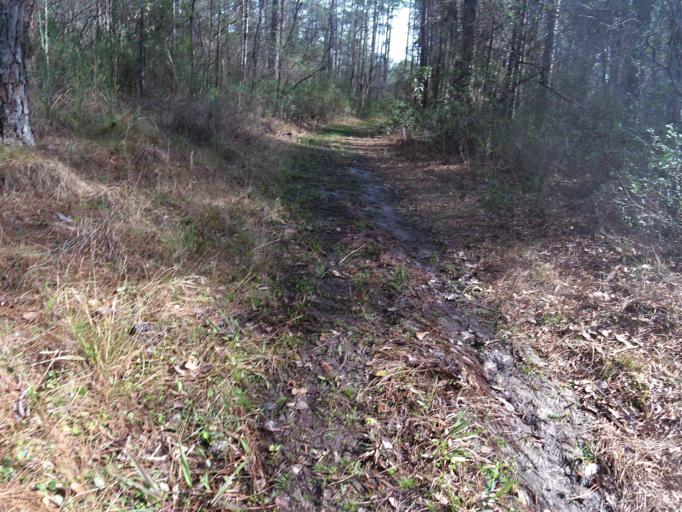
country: US
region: Florida
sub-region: Clay County
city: Middleburg
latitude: 30.1213
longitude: -81.9074
